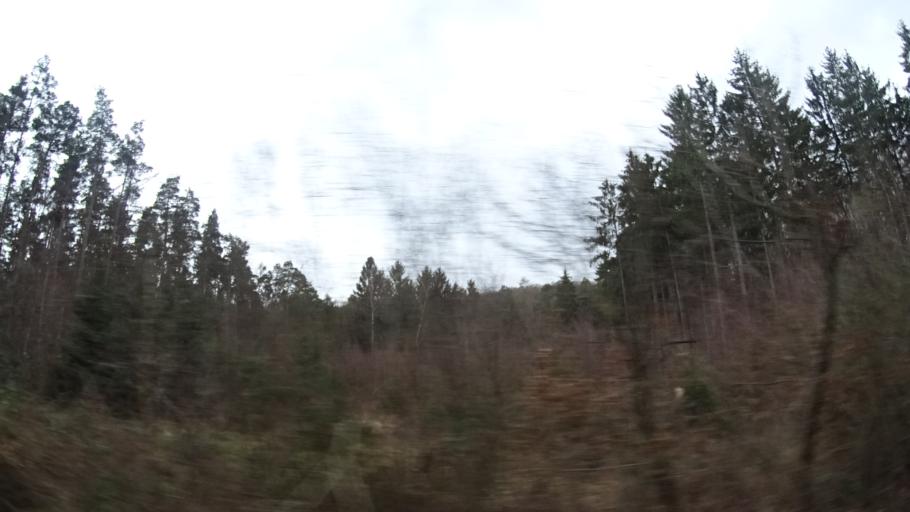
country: DE
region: Rheinland-Pfalz
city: Waldalgesheim
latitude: 49.9797
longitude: 7.8240
